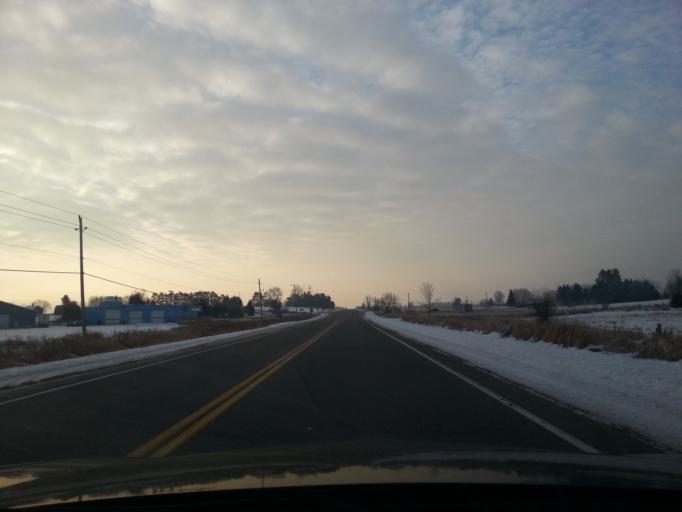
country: CA
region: Ontario
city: Perth
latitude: 44.9993
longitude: -76.2291
